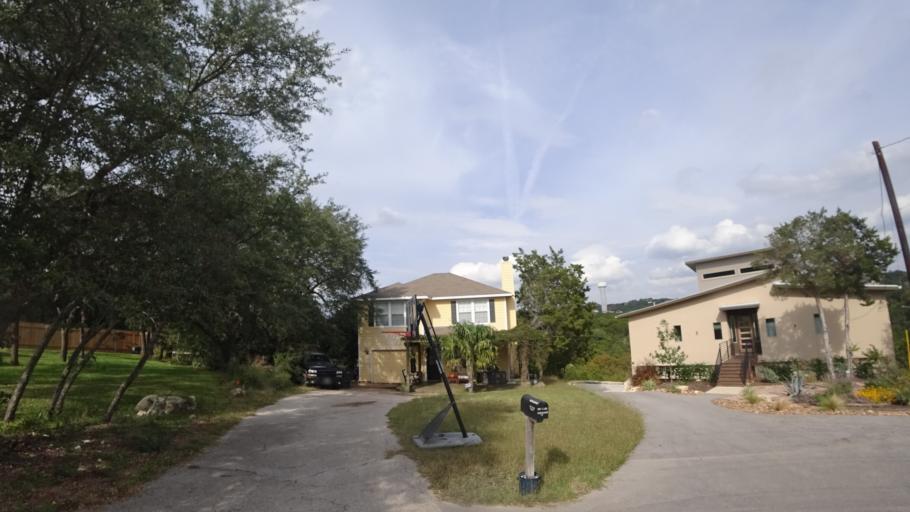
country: US
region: Texas
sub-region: Travis County
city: Hudson Bend
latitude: 30.3876
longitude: -97.9255
